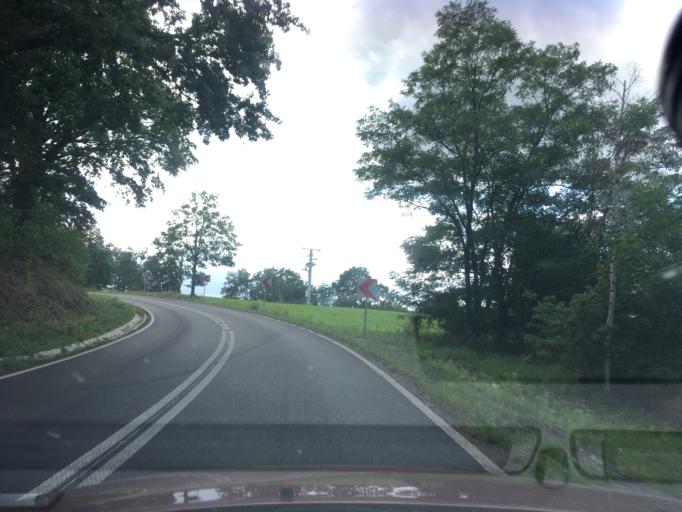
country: PL
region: Lower Silesian Voivodeship
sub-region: Powiat zgorzelecki
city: Piensk
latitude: 51.2191
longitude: 15.0217
